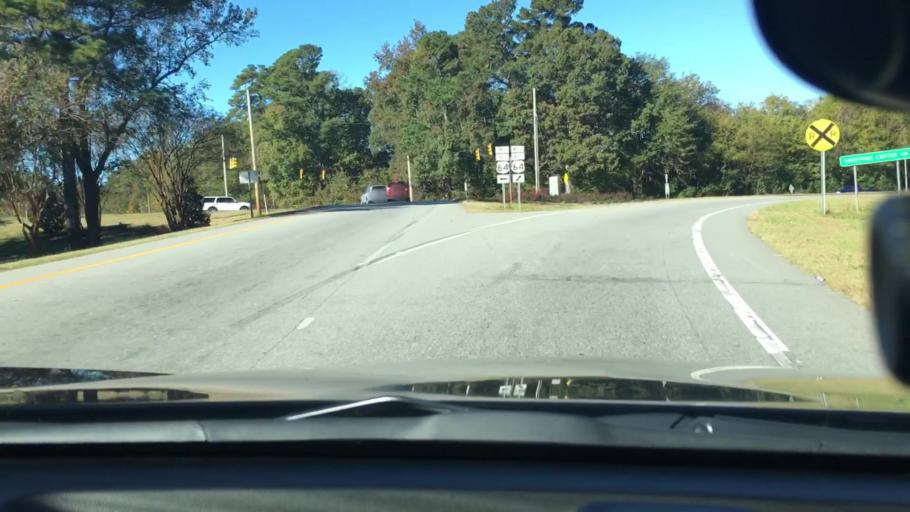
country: US
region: North Carolina
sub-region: Edgecombe County
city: Tarboro
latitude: 35.8878
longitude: -77.5466
